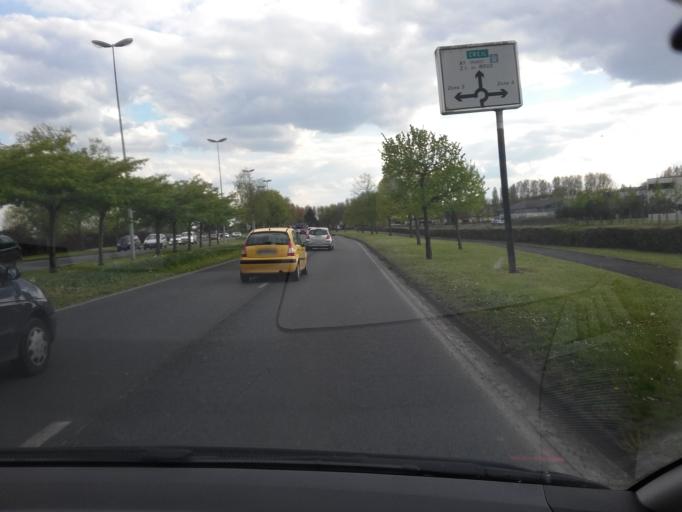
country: FR
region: Picardie
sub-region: Departement de l'Oise
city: Jaux
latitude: 49.3907
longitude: 2.7880
